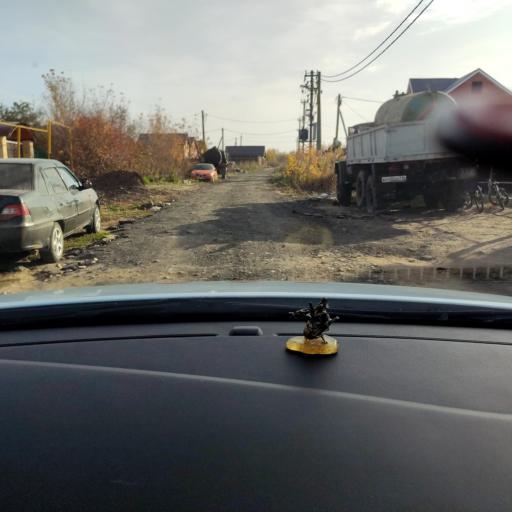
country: RU
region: Tatarstan
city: Vysokaya Gora
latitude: 55.7952
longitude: 49.2695
